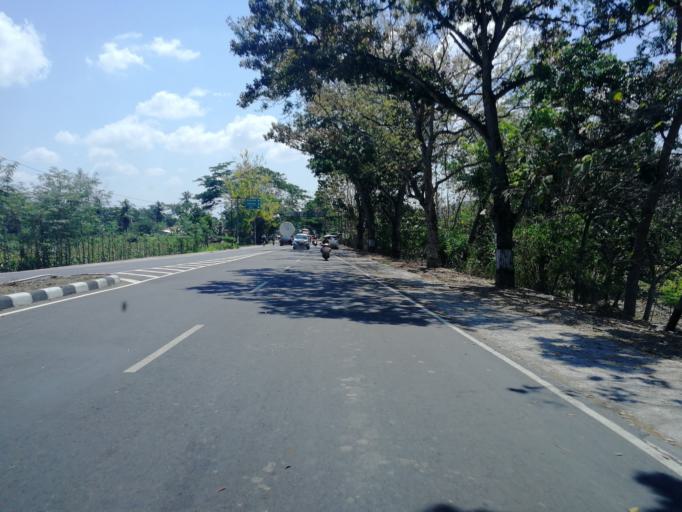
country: ID
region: West Nusa Tenggara
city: Kediri
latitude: -8.6896
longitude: 116.1142
